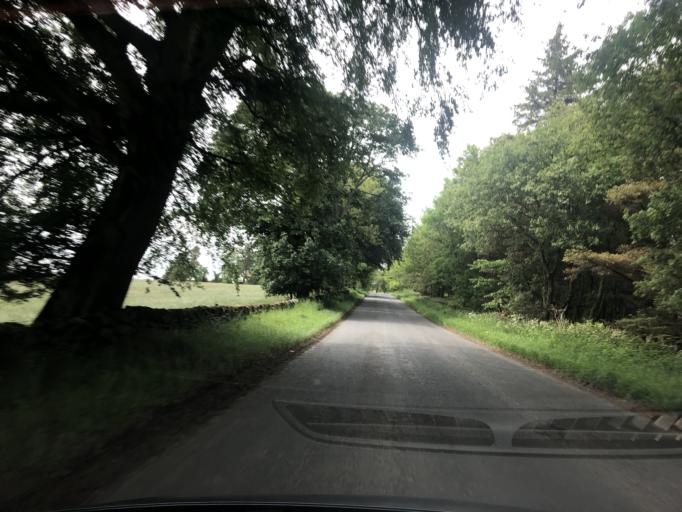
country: GB
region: Scotland
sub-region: The Scottish Borders
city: West Linton
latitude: 55.7378
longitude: -3.3334
